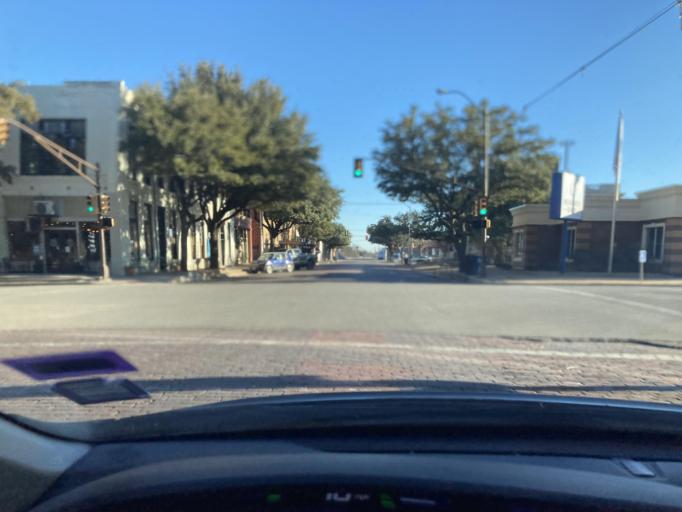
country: US
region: Texas
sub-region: Navarro County
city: Corsicana
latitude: 32.0931
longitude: -96.4649
